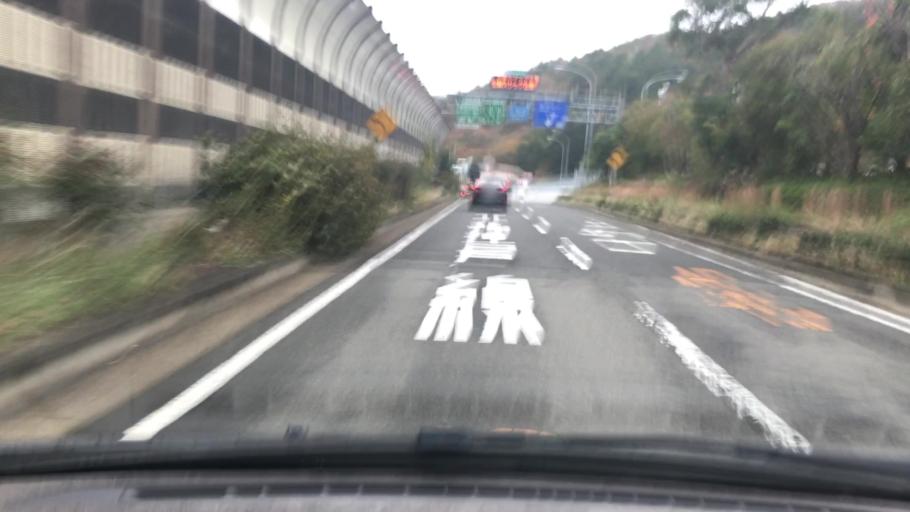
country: JP
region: Hyogo
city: Kobe
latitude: 34.7582
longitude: 135.1600
